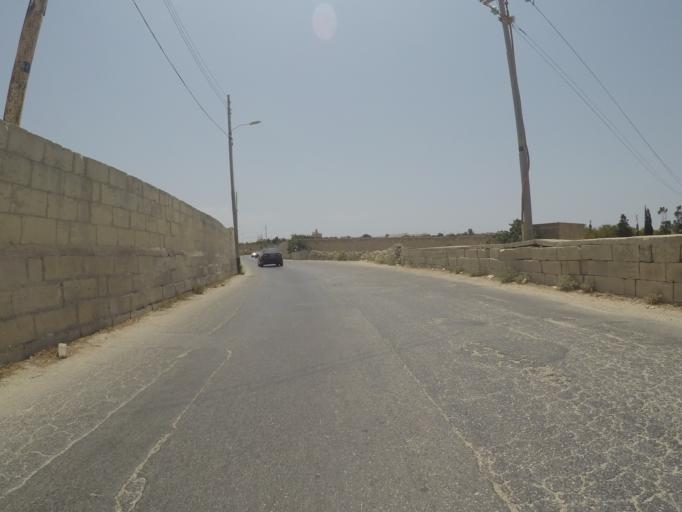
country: MT
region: Is-Siggiewi
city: Siggiewi
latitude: 35.8457
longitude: 14.4336
